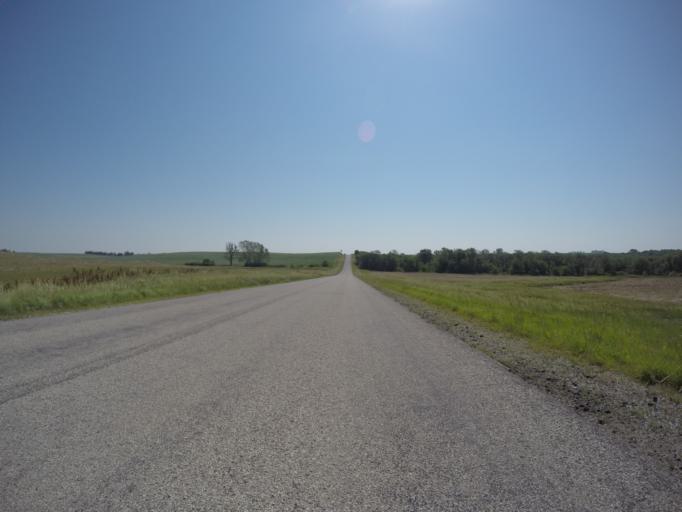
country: US
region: Kansas
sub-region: Doniphan County
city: Highland
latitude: 39.8565
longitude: -95.3742
